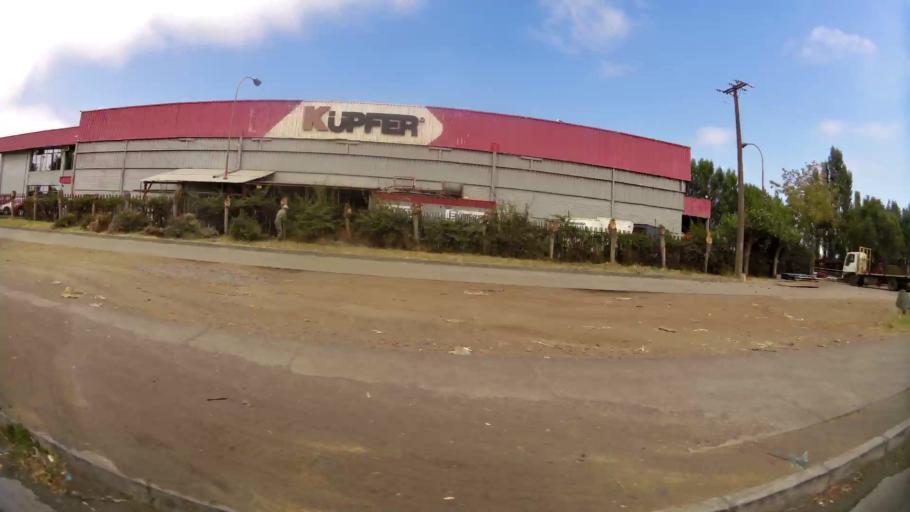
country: CL
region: Biobio
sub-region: Provincia de Concepcion
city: Concepcion
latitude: -36.7994
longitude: -73.0543
